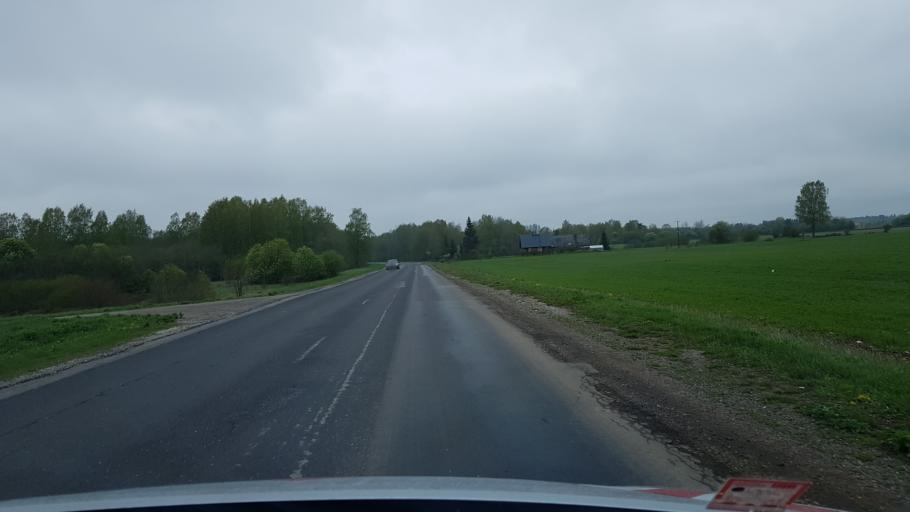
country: EE
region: Harju
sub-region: Raasiku vald
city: Raasiku
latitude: 59.3415
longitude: 25.1364
